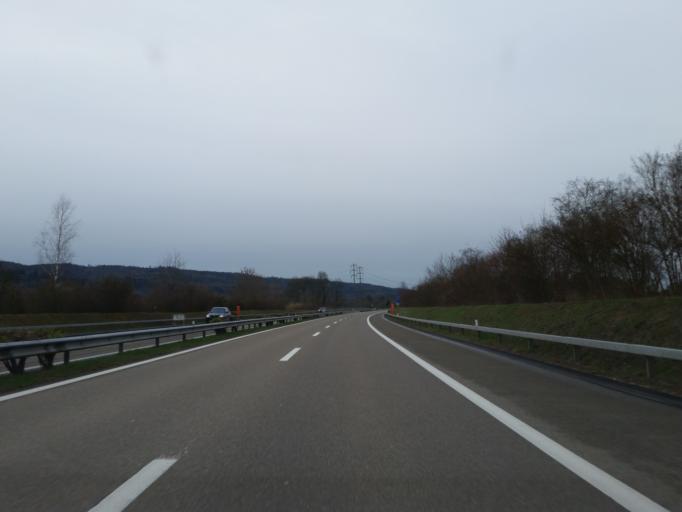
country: CH
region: Thurgau
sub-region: Frauenfeld District
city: Mullheim
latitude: 47.5941
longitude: 9.0060
